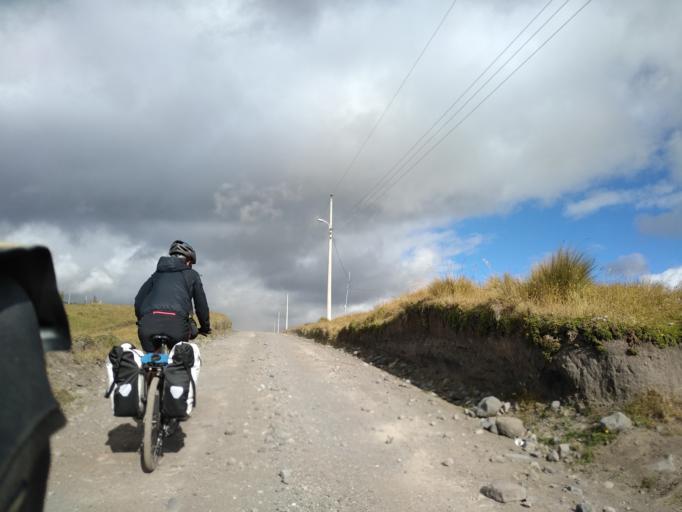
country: EC
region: Pichincha
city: Machachi
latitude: -0.5577
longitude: -78.4535
